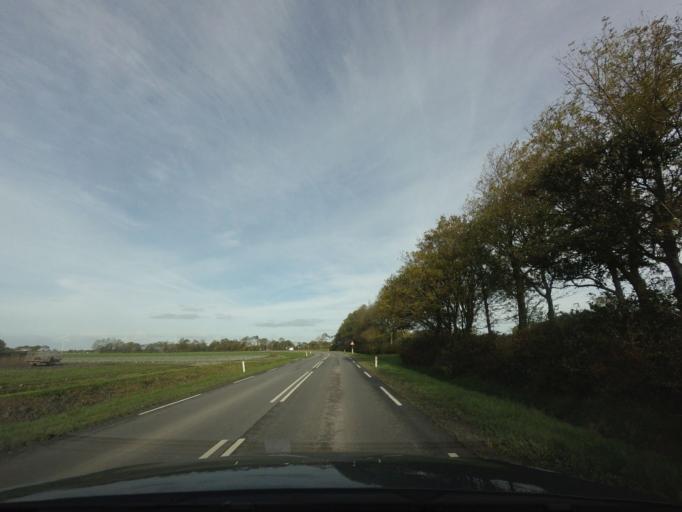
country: NL
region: North Holland
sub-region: Gemeente Schagen
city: Harenkarspel
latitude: 52.7157
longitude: 4.7942
